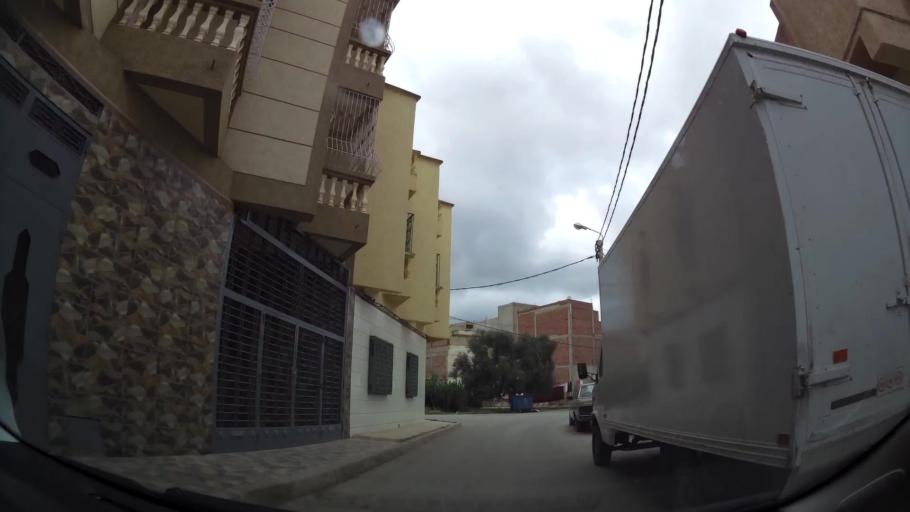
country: MA
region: Oriental
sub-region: Nador
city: Nador
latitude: 35.1634
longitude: -2.9388
